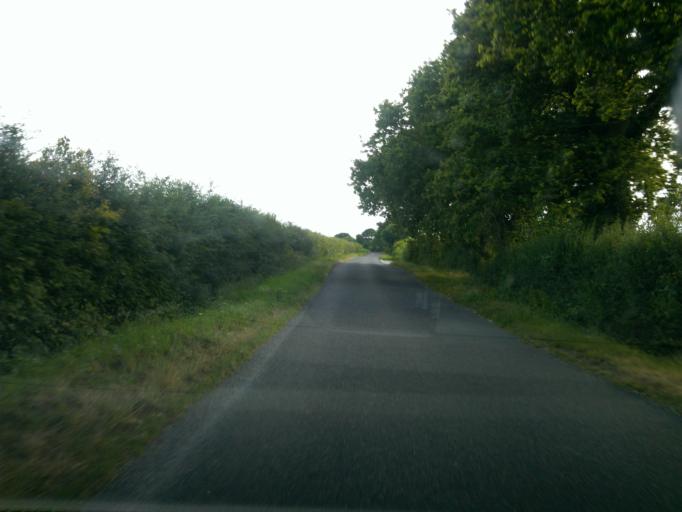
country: GB
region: England
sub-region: Essex
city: Great Bentley
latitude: 51.8398
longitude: 1.0856
